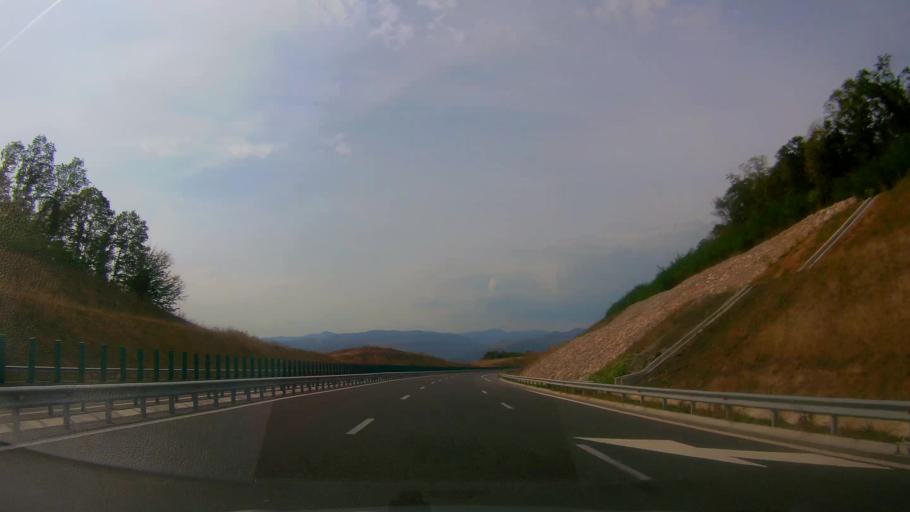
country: RO
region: Cluj
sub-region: Comuna Floresti
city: Luna de Sus
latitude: 46.7812
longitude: 23.4149
